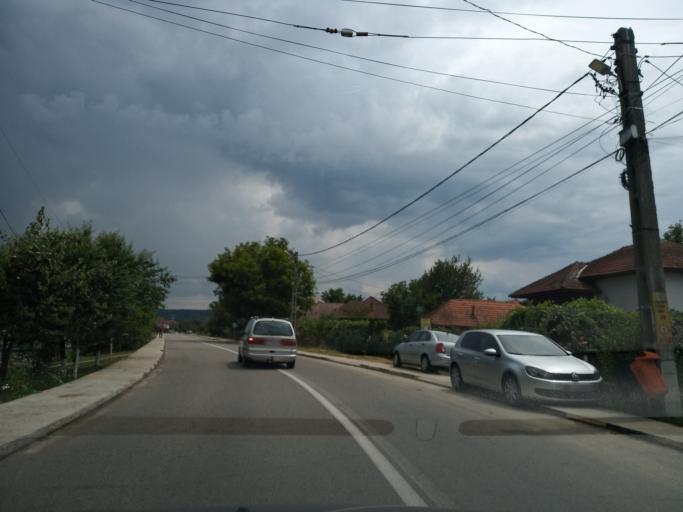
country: RO
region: Gorj
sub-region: Comuna Tismana
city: Tismana
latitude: 45.0464
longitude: 22.9484
